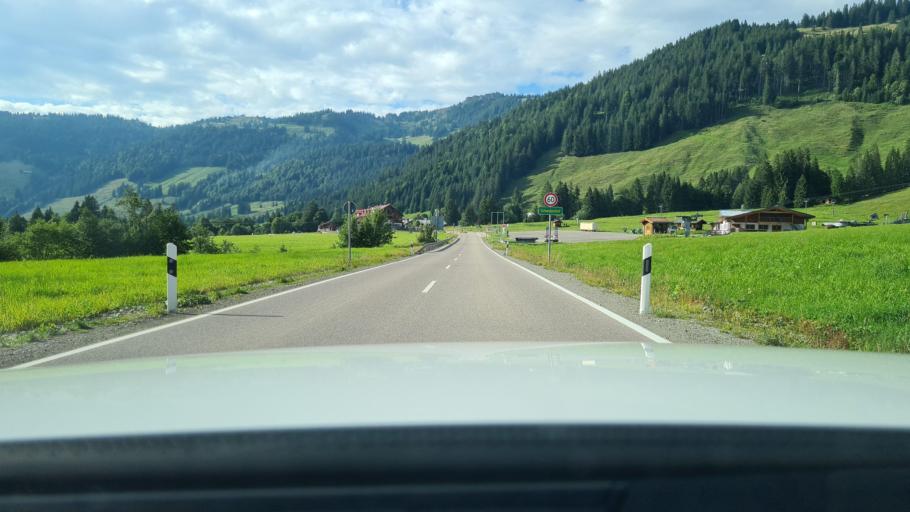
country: DE
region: Bavaria
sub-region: Swabia
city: Balderschwang
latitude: 47.4551
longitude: 10.1313
